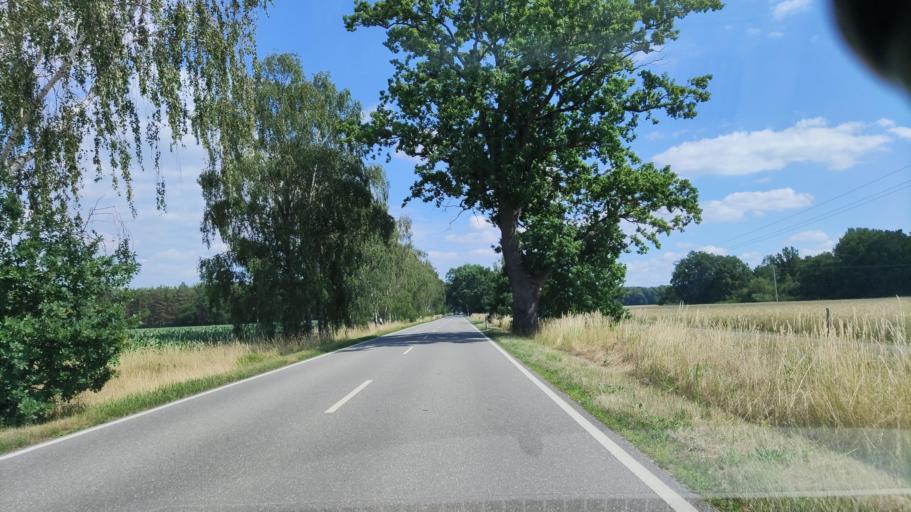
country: DE
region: Mecklenburg-Vorpommern
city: Lubtheen
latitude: 53.2680
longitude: 11.0923
